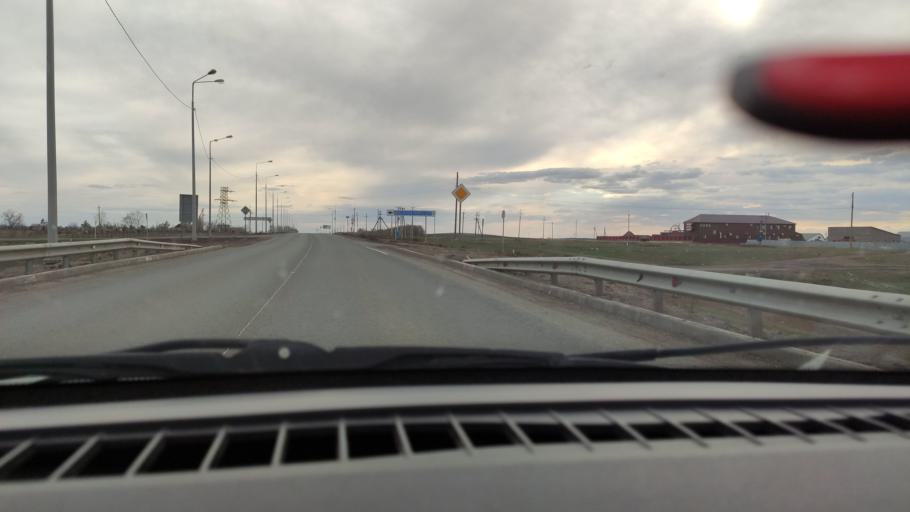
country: RU
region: Orenburg
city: Sakmara
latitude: 52.3306
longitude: 55.5028
